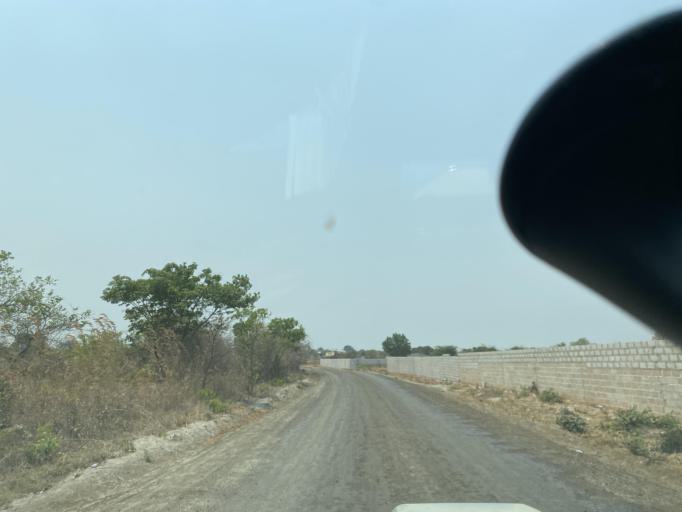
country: ZM
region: Lusaka
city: Lusaka
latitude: -15.5526
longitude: 28.4439
